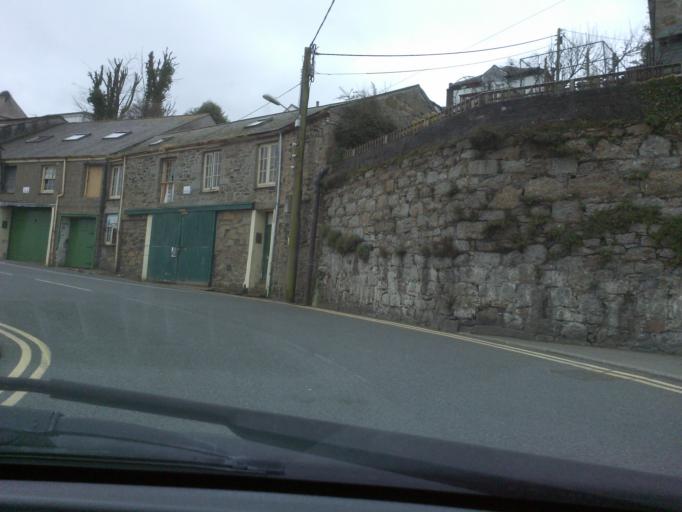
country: GB
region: England
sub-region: Cornwall
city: Penzance
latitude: 50.1034
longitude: -5.5496
